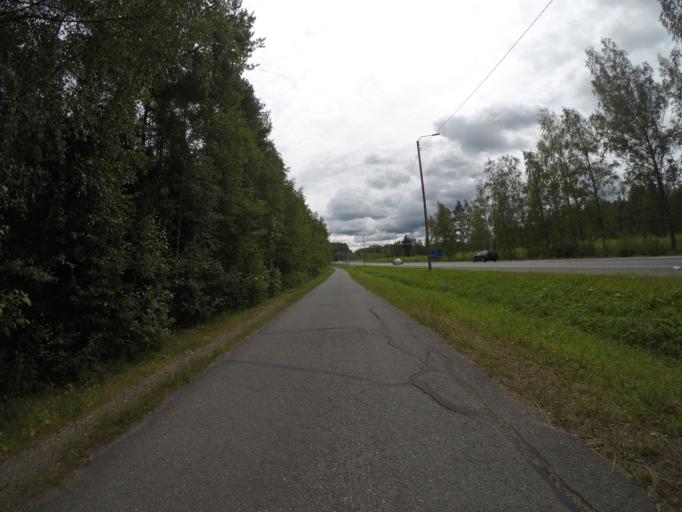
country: FI
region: Haeme
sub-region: Haemeenlinna
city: Haemeenlinna
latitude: 60.9867
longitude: 24.5043
